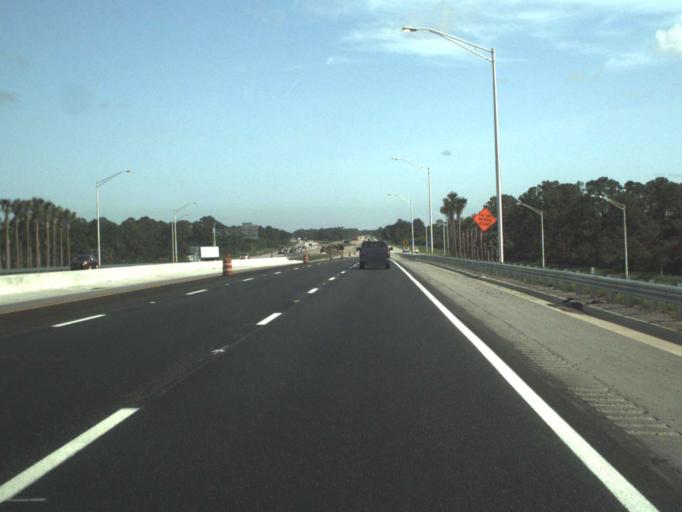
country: US
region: Florida
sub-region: Indian River County
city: West Vero Corridor
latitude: 27.6412
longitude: -80.5184
